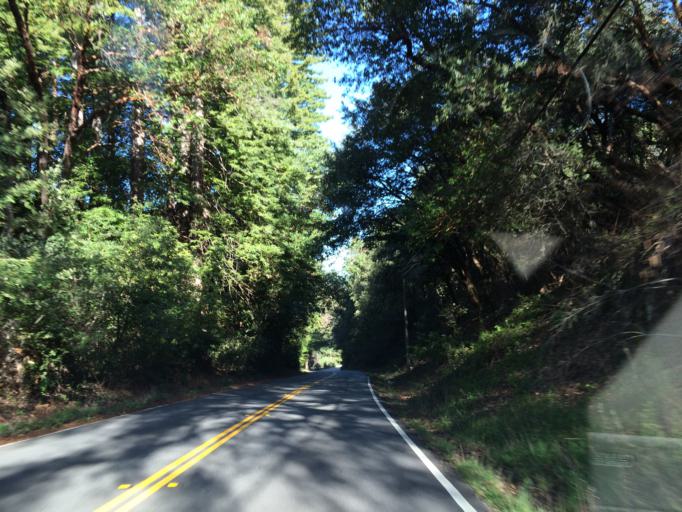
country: US
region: California
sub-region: Santa Cruz County
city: Boulder Creek
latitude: 37.1336
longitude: -122.1697
